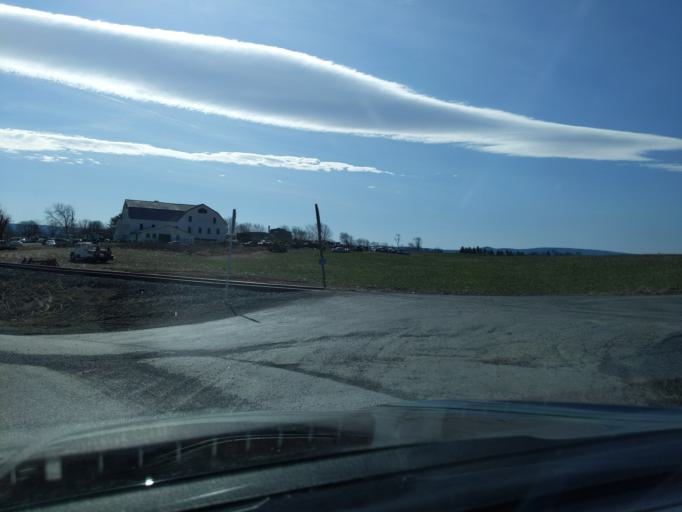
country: US
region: Pennsylvania
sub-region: Blair County
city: Martinsburg
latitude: 40.3125
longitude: -78.3447
